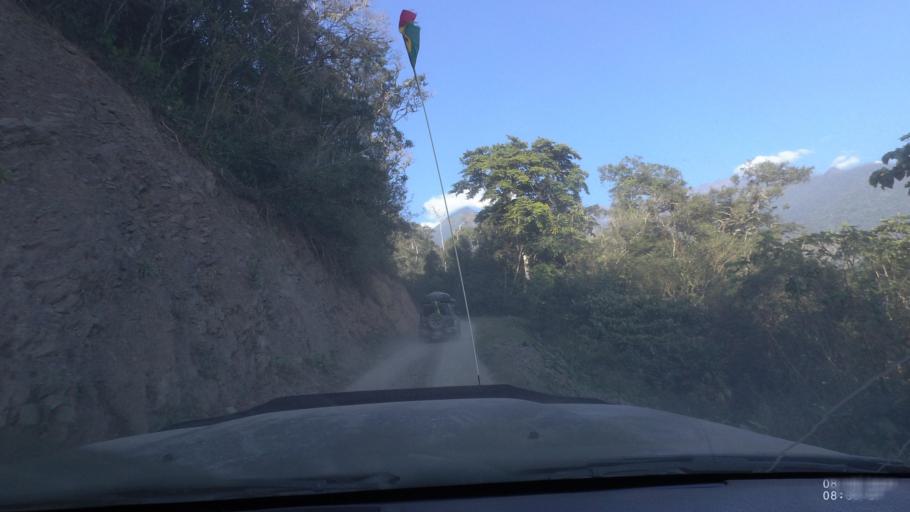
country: BO
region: La Paz
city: Quime
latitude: -16.5146
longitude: -66.7661
